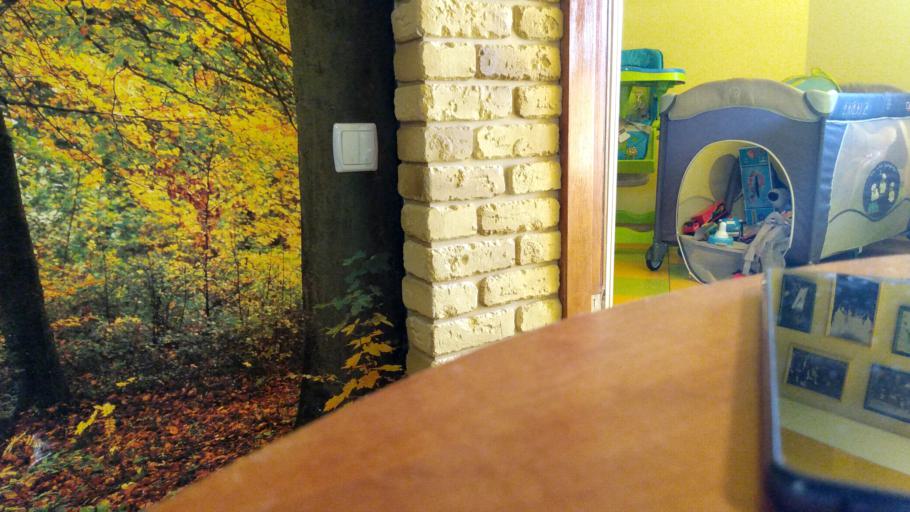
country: RU
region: Tverskaya
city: Kalashnikovo
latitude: 57.3679
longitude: 35.2158
